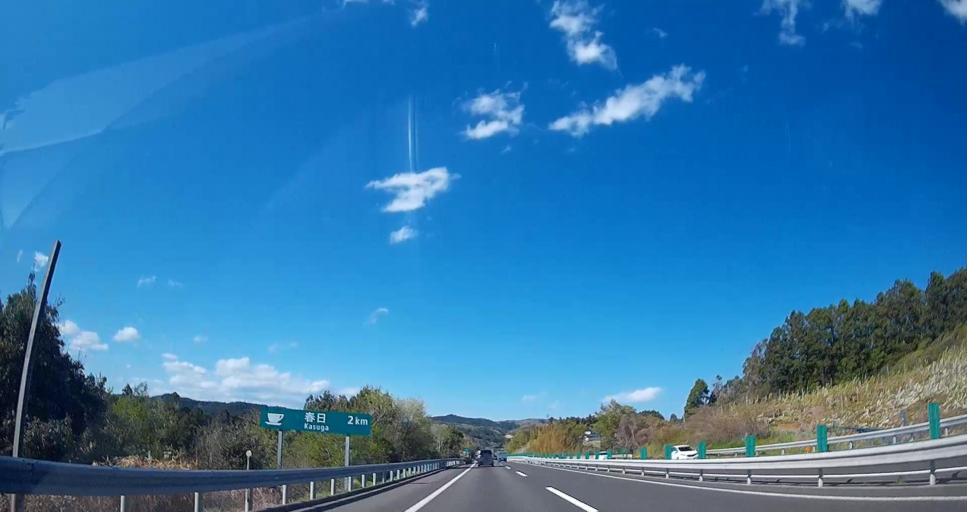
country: JP
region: Miyagi
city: Rifu
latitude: 38.3322
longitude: 140.9966
